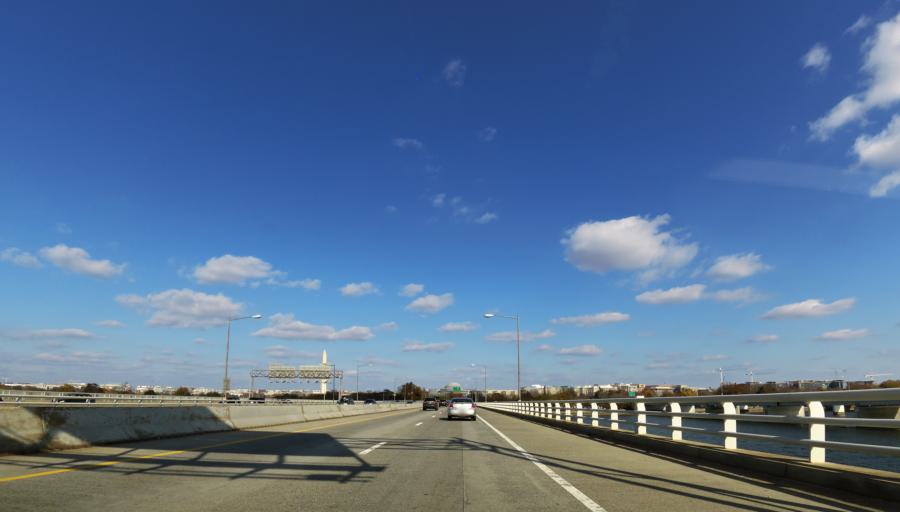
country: US
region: Washington, D.C.
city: Washington, D.C.
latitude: 38.8759
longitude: -77.0413
